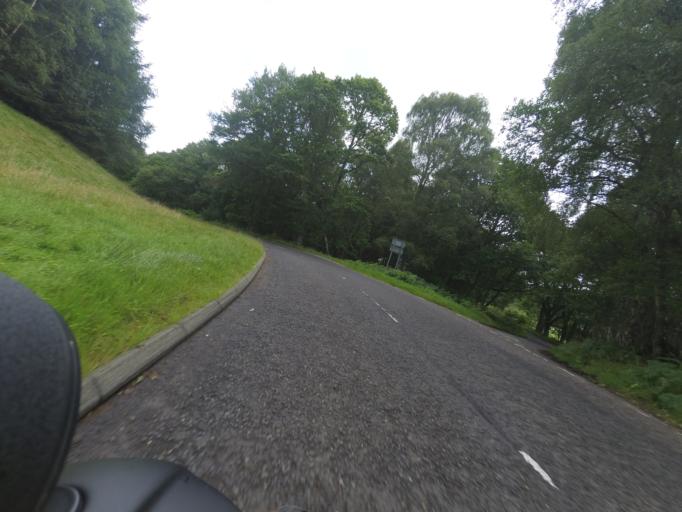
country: GB
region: Scotland
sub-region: Perth and Kinross
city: Bankfoot
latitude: 56.5743
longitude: -3.5675
